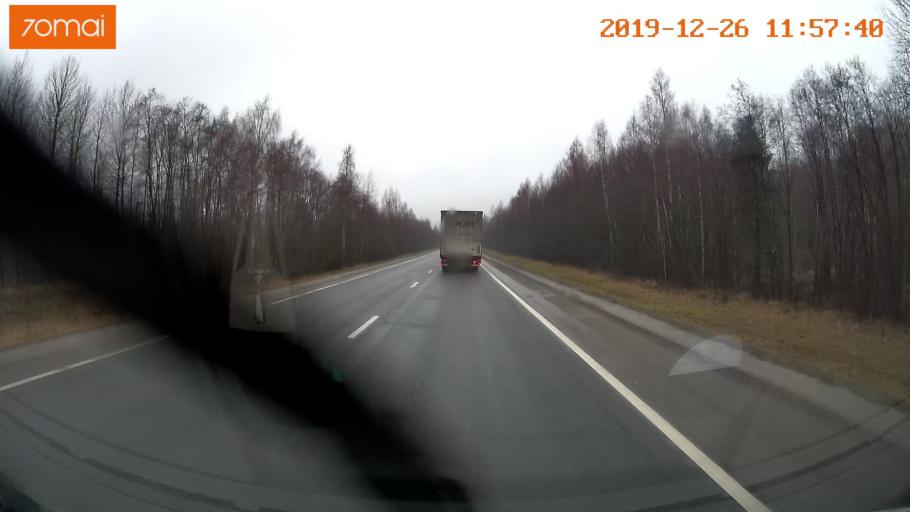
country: RU
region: Vologda
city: Sheksna
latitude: 59.2902
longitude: 38.2460
